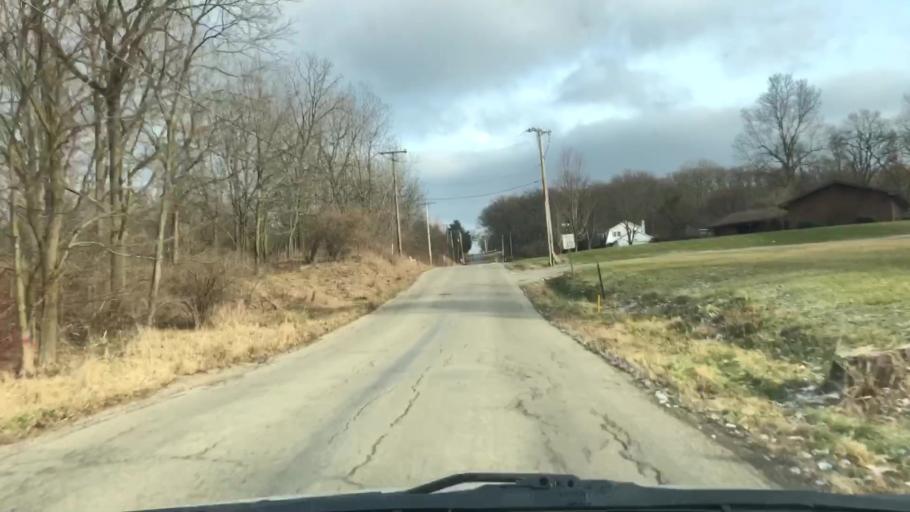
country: US
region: Indiana
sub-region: Steuben County
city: Angola
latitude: 41.6826
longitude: -85.0127
